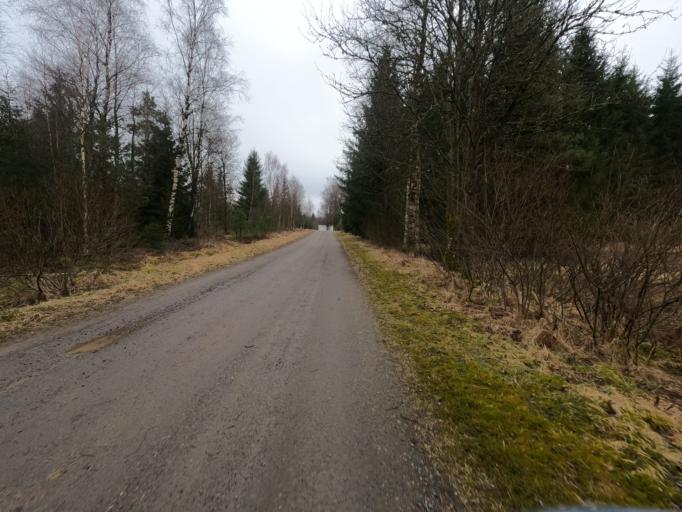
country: SE
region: Kronoberg
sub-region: Markaryds Kommun
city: Stromsnasbruk
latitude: 56.7906
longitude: 13.5583
